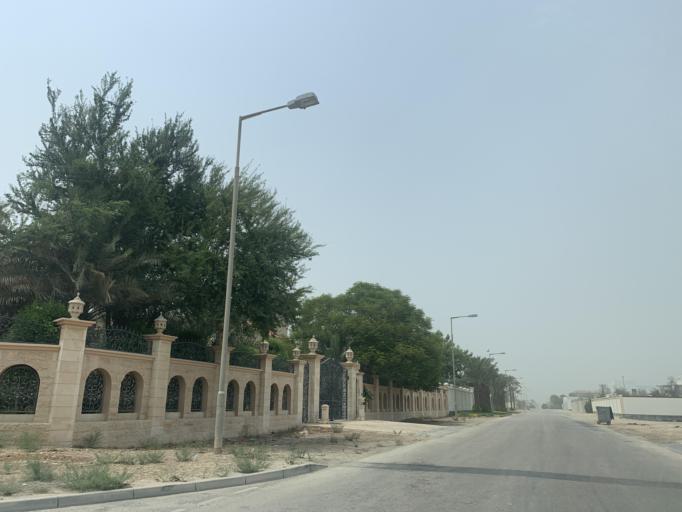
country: BH
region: Central Governorate
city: Madinat Hamad
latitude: 26.1608
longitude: 50.4768
